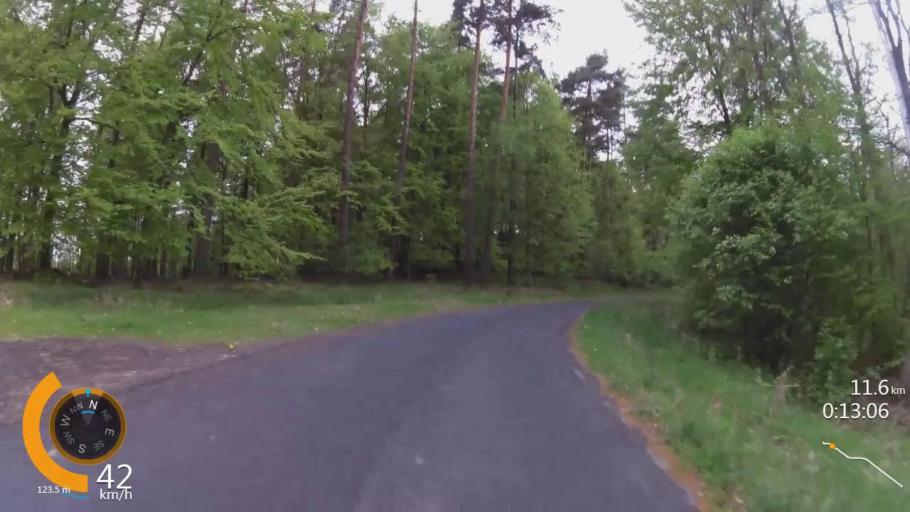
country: PL
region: West Pomeranian Voivodeship
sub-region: Powiat drawski
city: Wierzchowo
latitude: 53.5244
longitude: 16.0977
